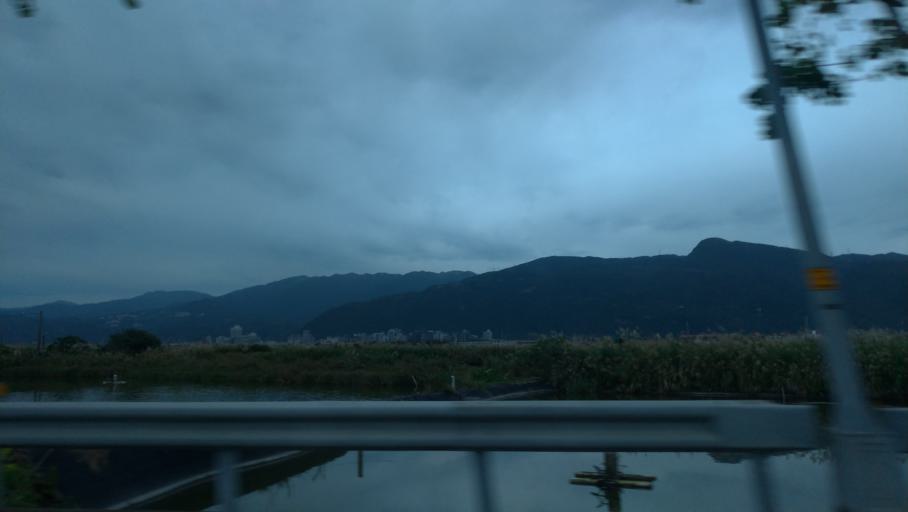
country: TW
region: Taiwan
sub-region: Yilan
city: Yilan
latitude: 24.8237
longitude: 121.7991
